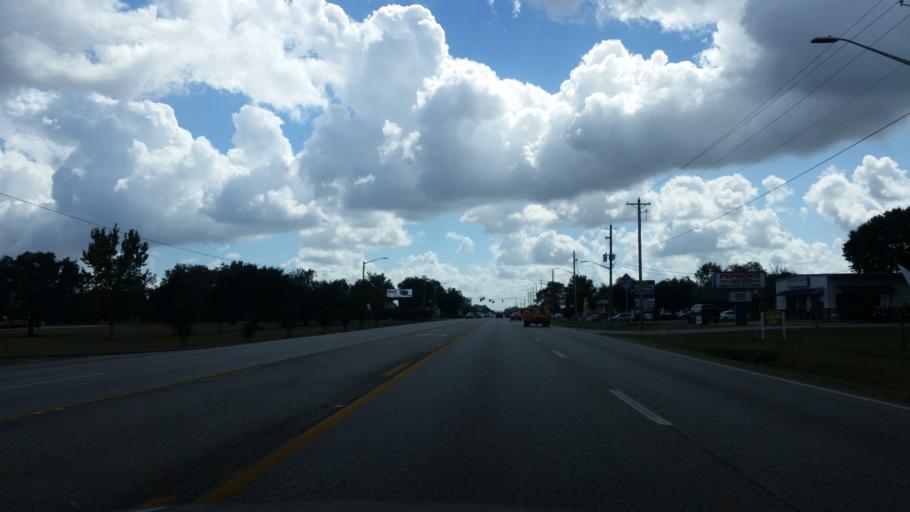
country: US
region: Alabama
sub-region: Baldwin County
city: Robertsdale
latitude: 30.5407
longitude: -87.7084
